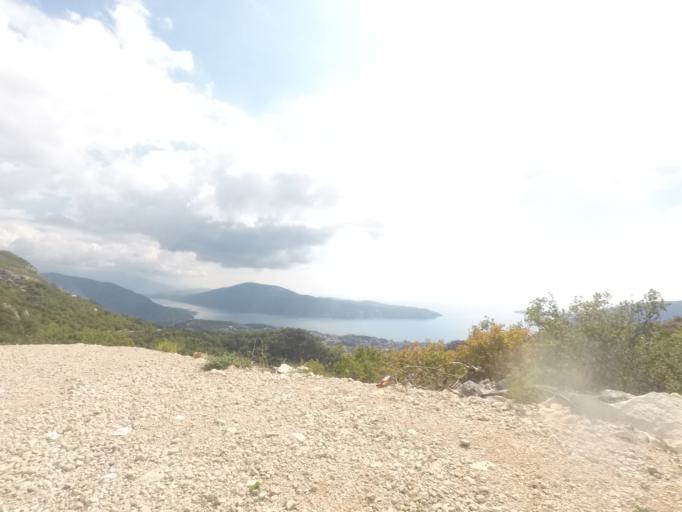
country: ME
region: Herceg Novi
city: Herceg-Novi
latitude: 42.4732
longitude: 18.5312
